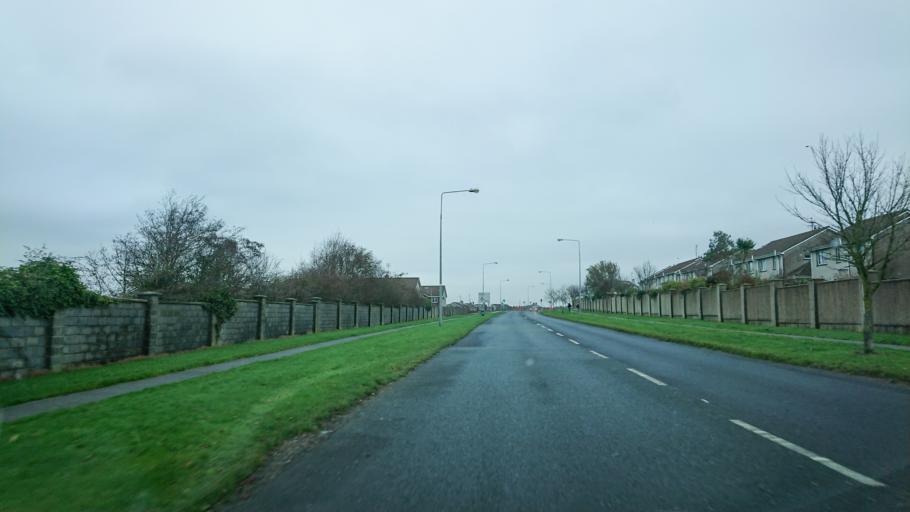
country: IE
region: Munster
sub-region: Waterford
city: Tra Mhor
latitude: 52.1644
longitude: -7.1652
